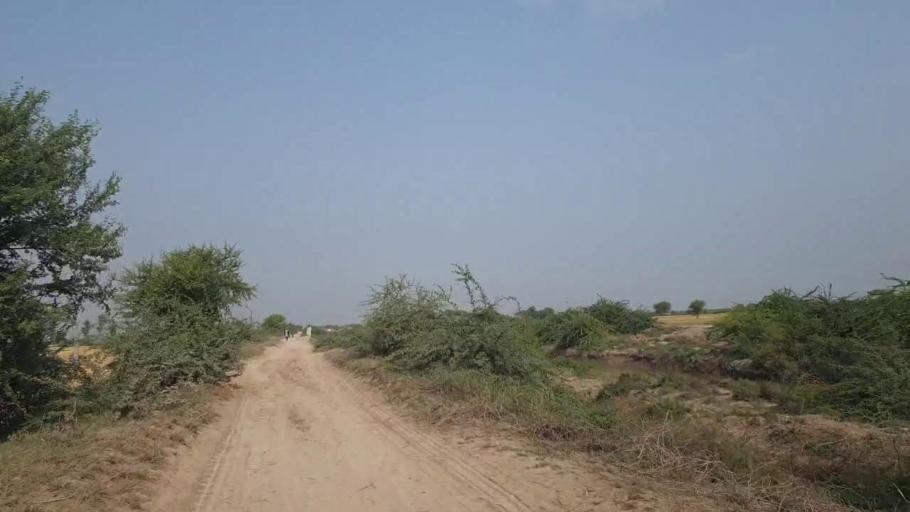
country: PK
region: Sindh
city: Badin
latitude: 24.7357
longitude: 68.7661
